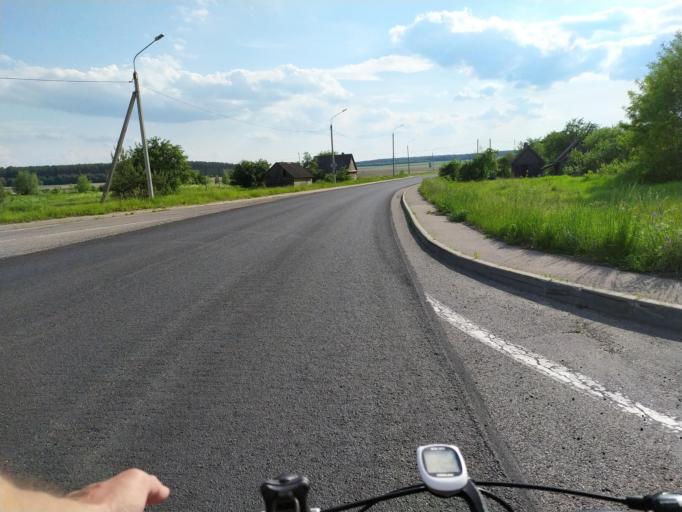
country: BY
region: Brest
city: Kamyanyets
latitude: 52.3944
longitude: 23.9849
